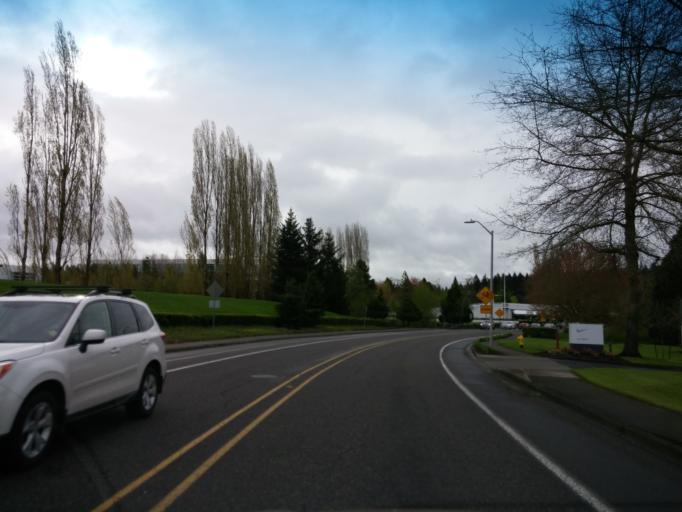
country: US
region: Oregon
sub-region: Washington County
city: Cedar Mill
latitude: 45.5085
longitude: -122.8345
